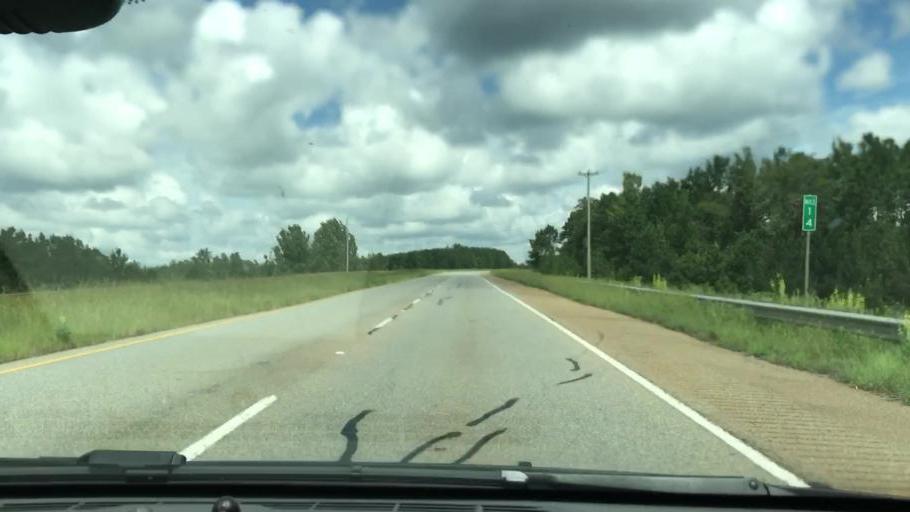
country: US
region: Georgia
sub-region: Stewart County
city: Lumpkin
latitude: 32.1093
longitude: -84.8137
